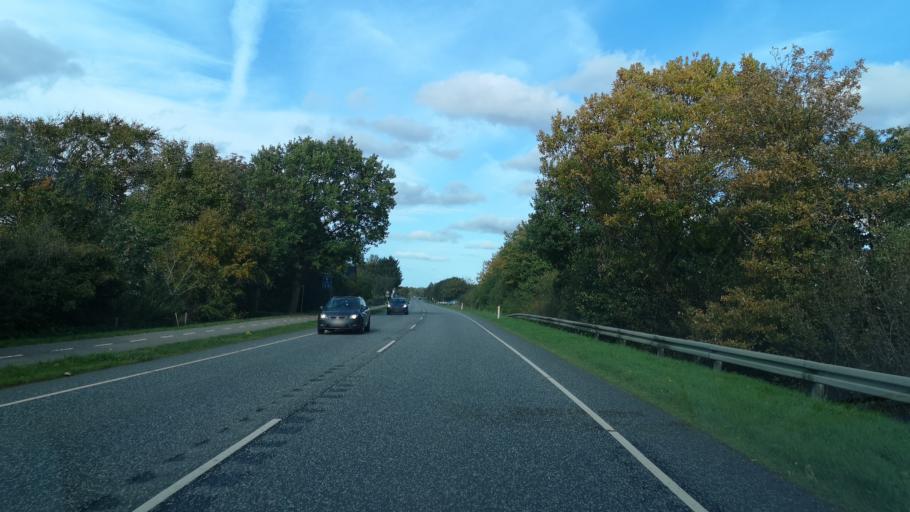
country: DK
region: Central Jutland
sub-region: Holstebro Kommune
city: Holstebro
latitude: 56.3277
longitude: 8.6106
